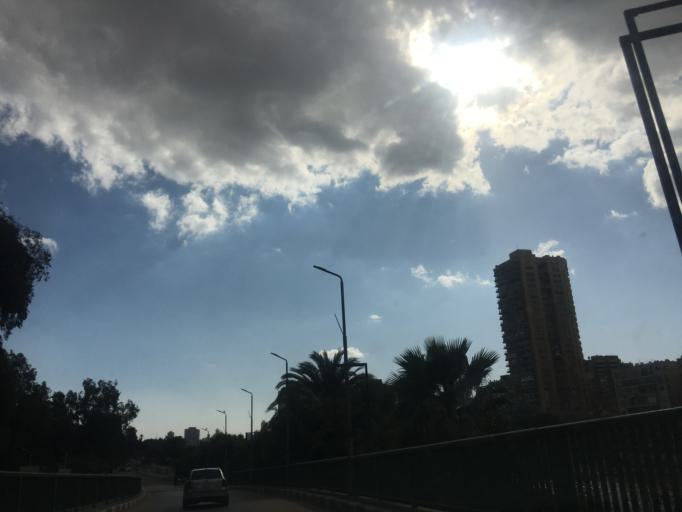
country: EG
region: Muhafazat al Qahirah
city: Cairo
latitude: 30.0478
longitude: 31.2195
